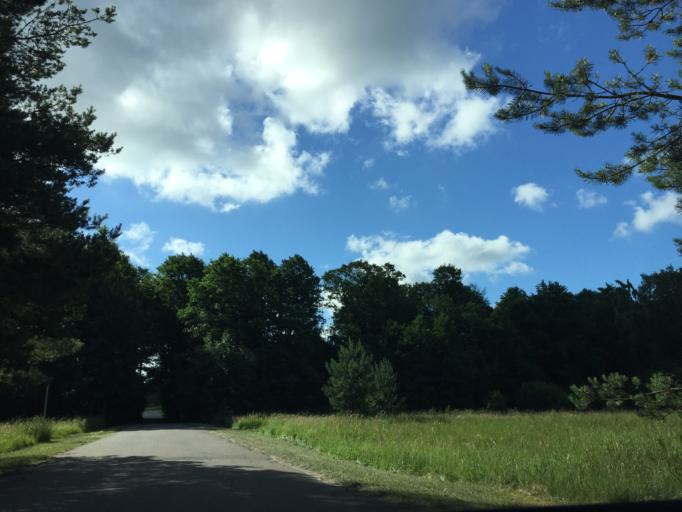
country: LV
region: Ventspils
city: Ventspils
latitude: 57.4435
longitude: 21.6059
